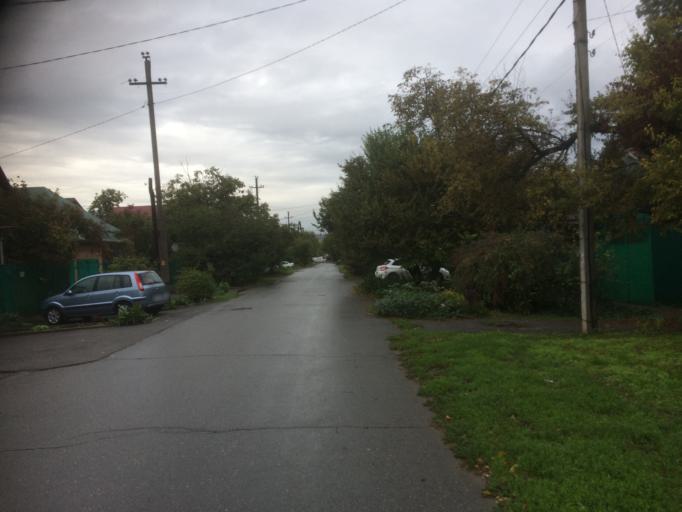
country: RU
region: Krasnodarskiy
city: Krasnodar
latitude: 45.0401
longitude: 38.9379
